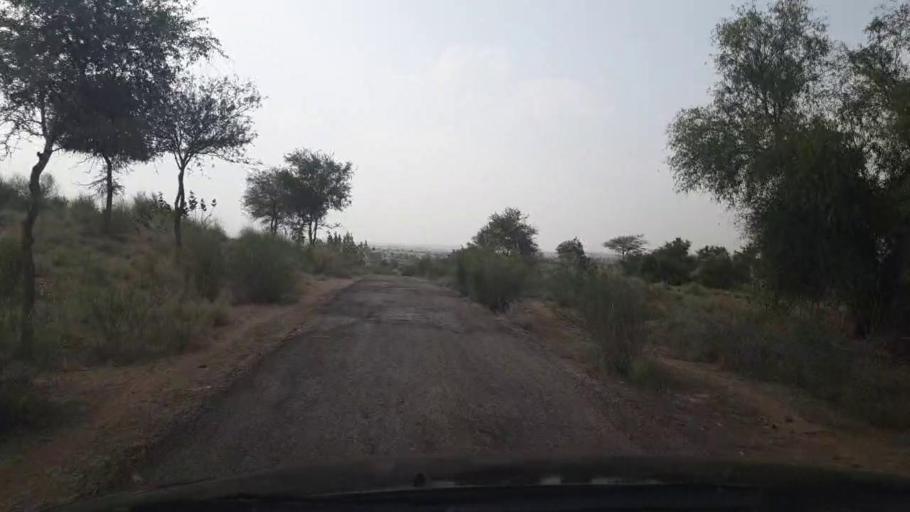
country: PK
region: Sindh
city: Islamkot
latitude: 24.9694
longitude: 70.5955
